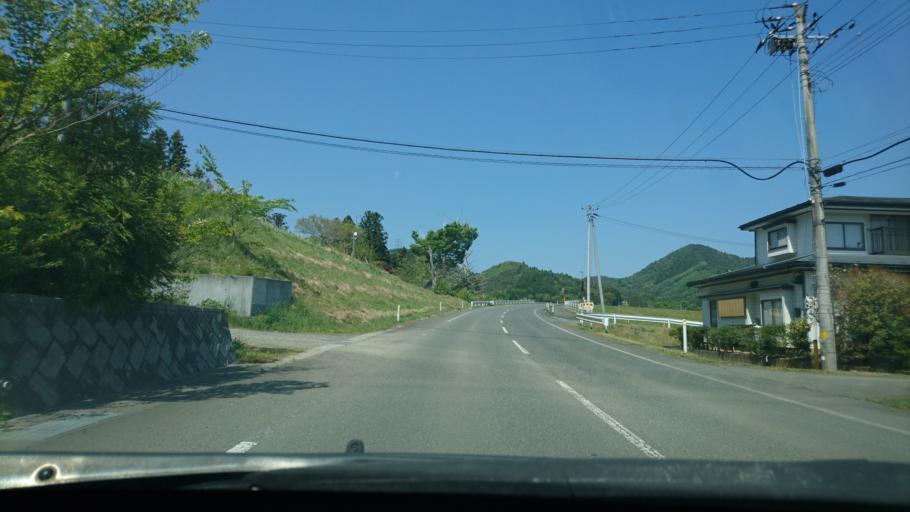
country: JP
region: Iwate
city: Ichinoseki
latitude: 38.9273
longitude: 141.2524
